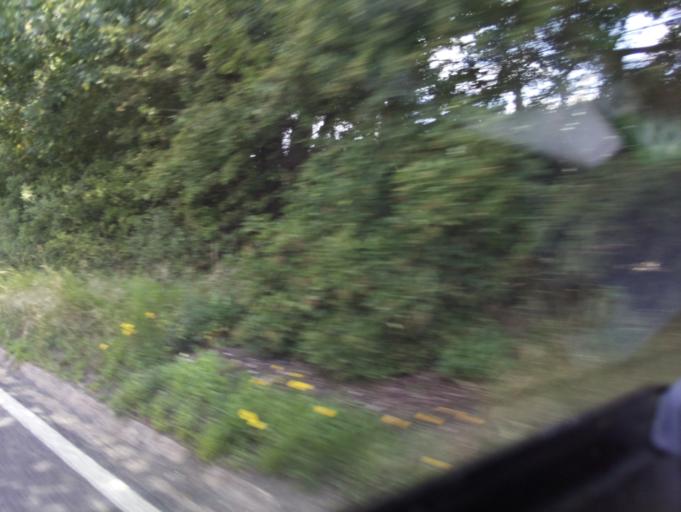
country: GB
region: England
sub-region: Buckinghamshire
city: Winslow
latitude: 51.8949
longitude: -0.8316
